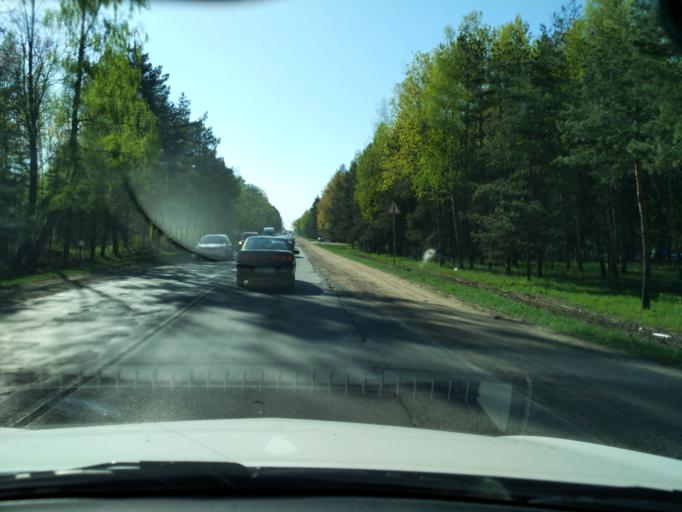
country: BY
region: Minsk
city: Borovlyany
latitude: 53.9655
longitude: 27.6611
